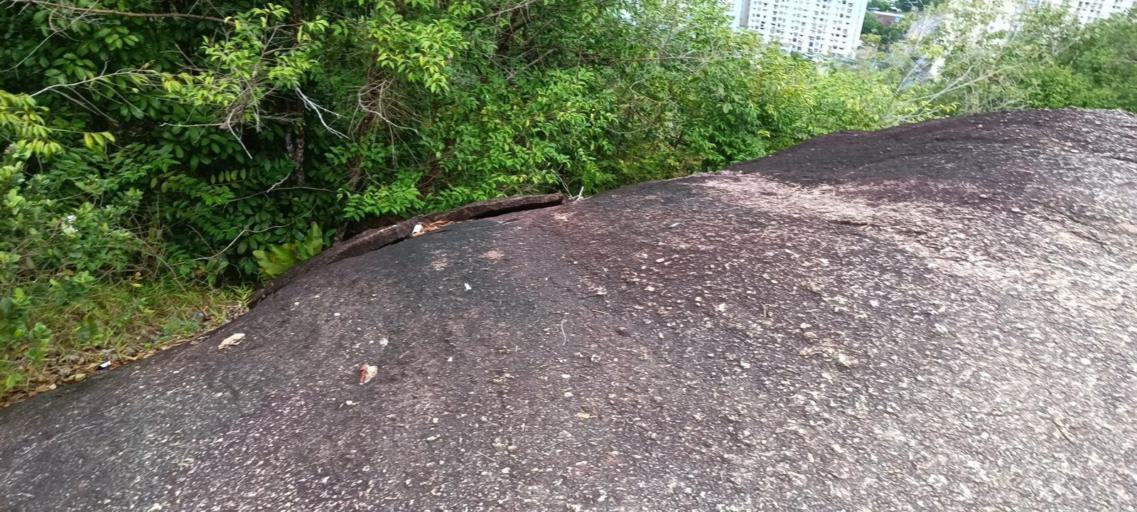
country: MY
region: Penang
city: George Town
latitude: 5.3888
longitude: 100.2909
